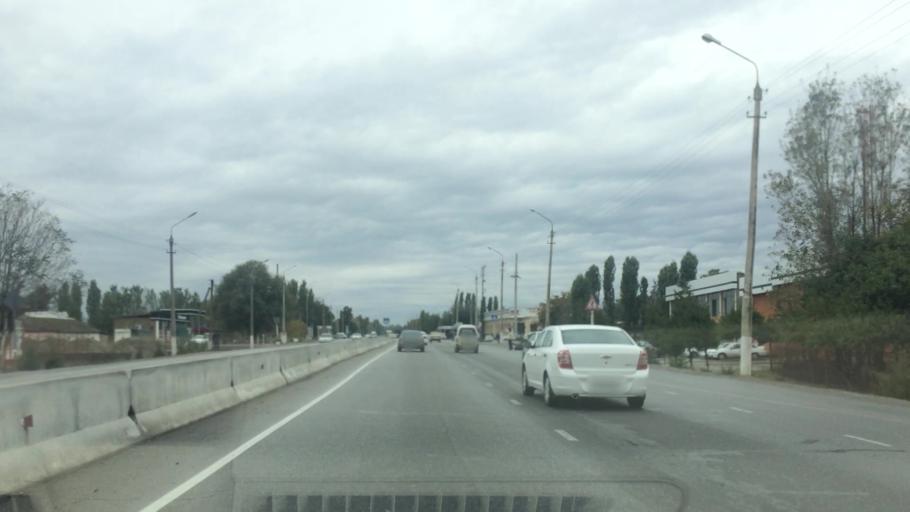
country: UZ
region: Jizzax
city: Jizzax
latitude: 40.0032
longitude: 67.5935
